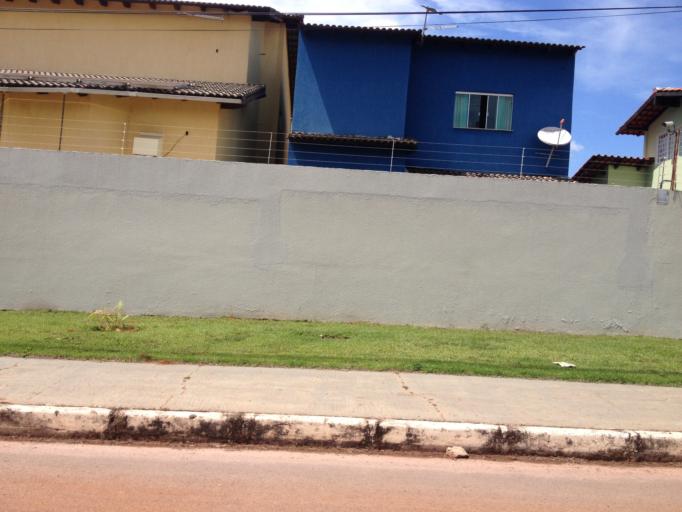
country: BR
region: Federal District
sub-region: Brasilia
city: Brasilia
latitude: -15.8291
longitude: -48.0303
